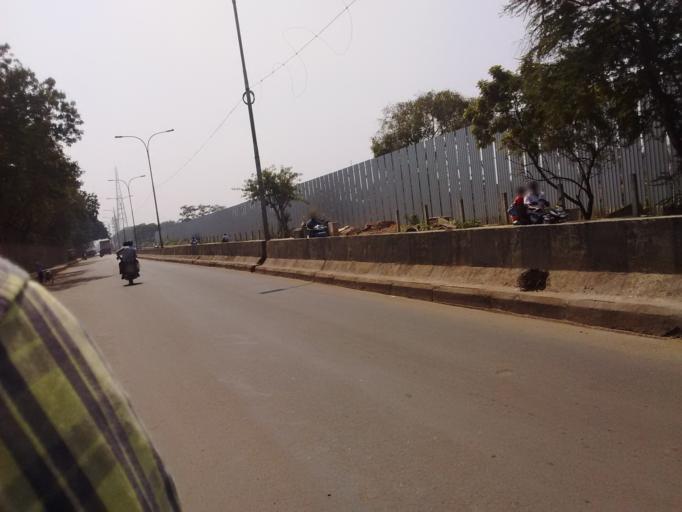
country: IN
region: Tamil Nadu
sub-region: Thiruvallur
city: Tiruvottiyur
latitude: 13.1784
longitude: 80.3071
